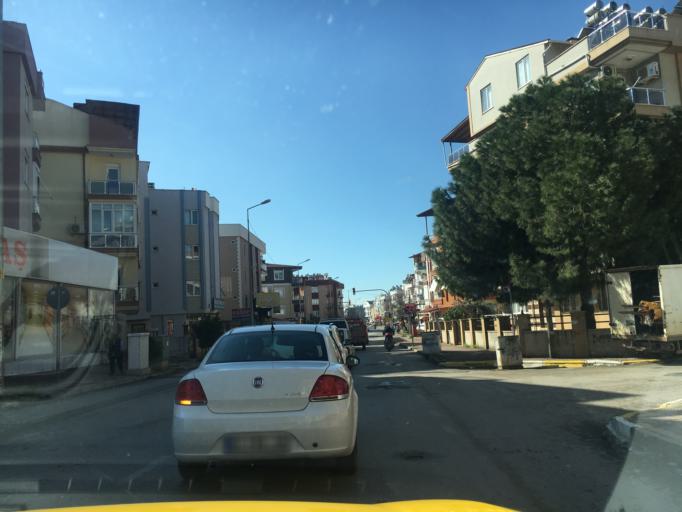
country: TR
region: Antalya
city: Antalya
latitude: 36.9159
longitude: 30.7067
